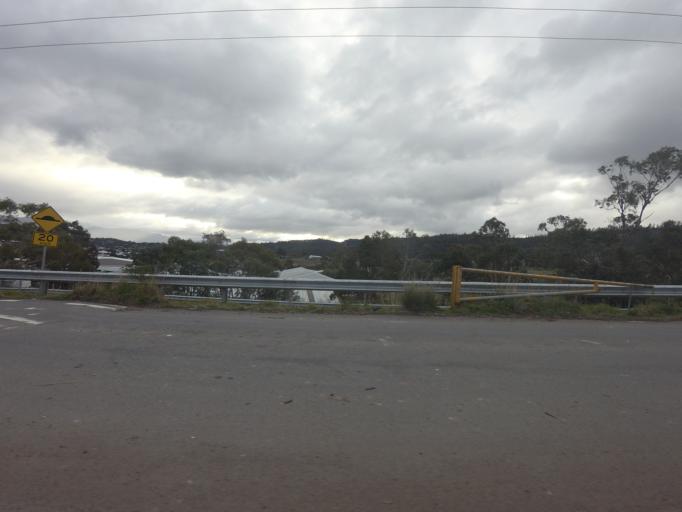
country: AU
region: Tasmania
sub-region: Clarence
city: Warrane
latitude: -42.8615
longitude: 147.4053
